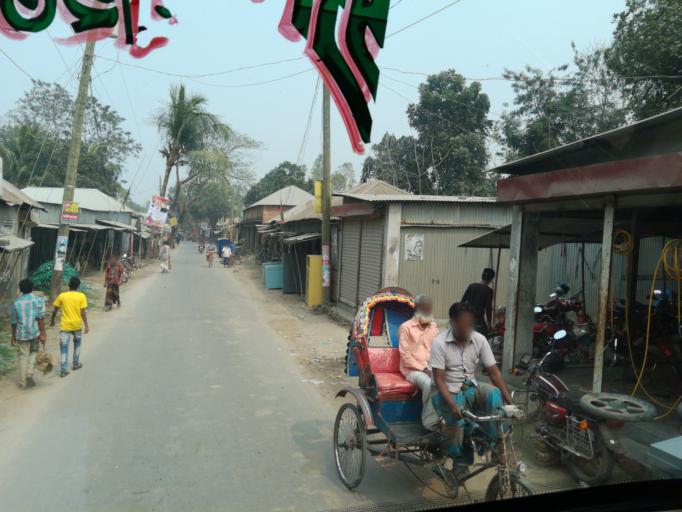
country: BD
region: Dhaka
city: Nagarpur
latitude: 23.9023
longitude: 89.8752
